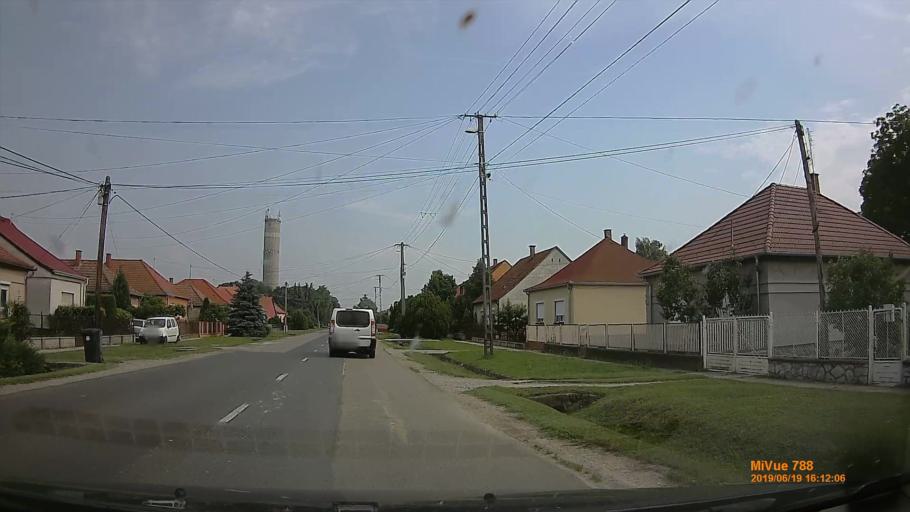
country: HU
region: Baranya
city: Szigetvar
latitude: 46.0521
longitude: 17.7827
